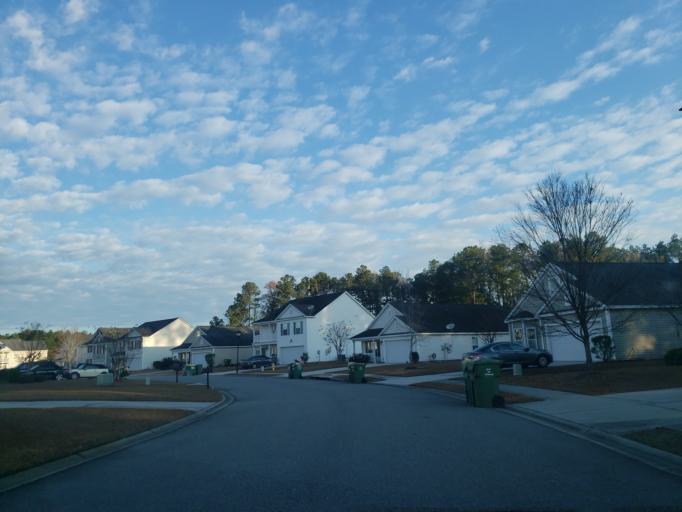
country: US
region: Georgia
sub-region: Chatham County
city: Bloomingdale
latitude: 32.1527
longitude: -81.2695
